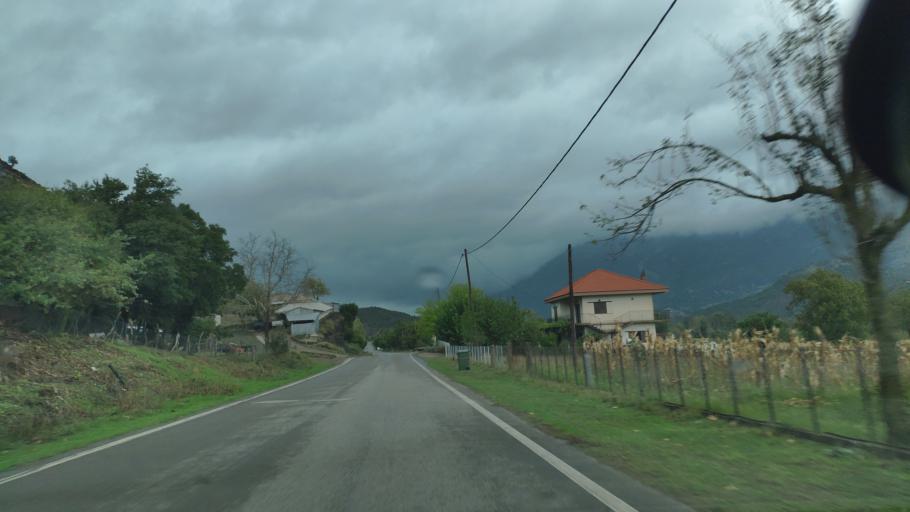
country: GR
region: West Greece
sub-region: Nomos Aitolias kai Akarnanias
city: Krikellos
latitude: 38.9958
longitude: 21.3127
